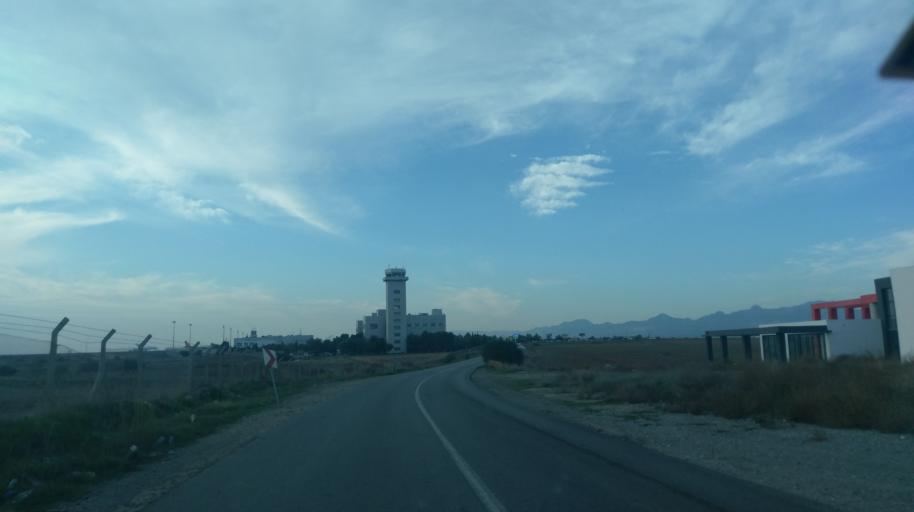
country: CY
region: Larnaka
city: Athienou
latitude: 35.1555
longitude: 33.5108
